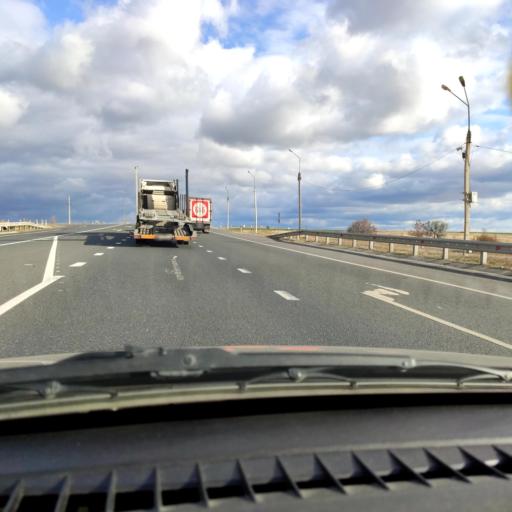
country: RU
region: Samara
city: Varlamovo
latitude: 53.2046
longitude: 48.3832
